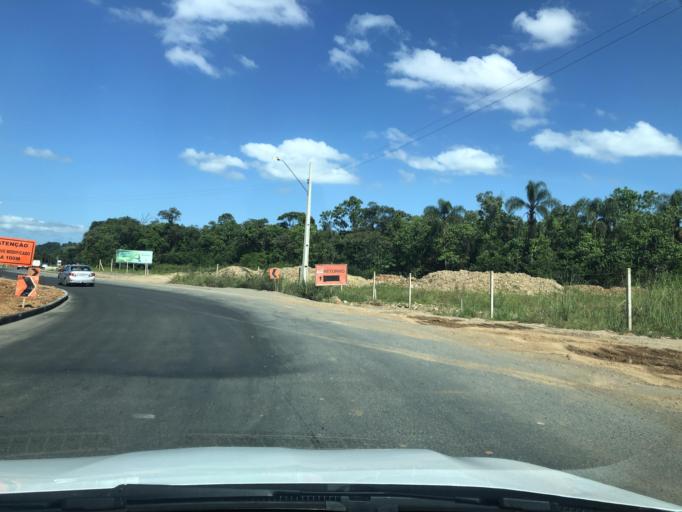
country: BR
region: Santa Catarina
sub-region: Joinville
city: Joinville
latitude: -26.2507
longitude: -48.8639
